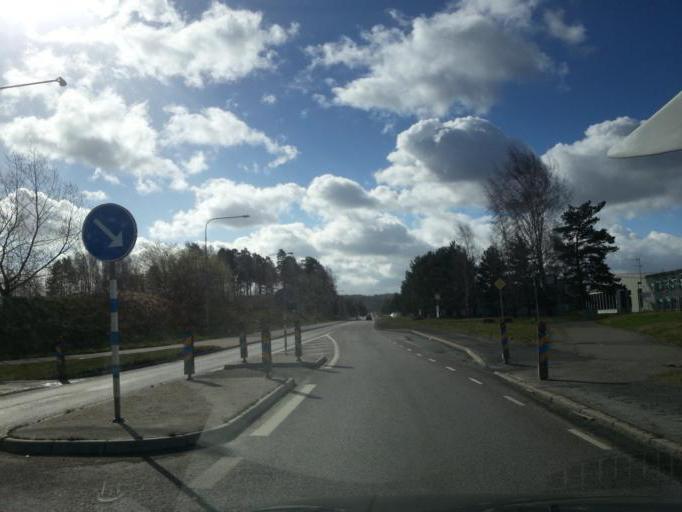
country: SE
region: Joenkoeping
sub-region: Jonkopings Kommun
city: Jonkoping
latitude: 57.7572
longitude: 14.1691
